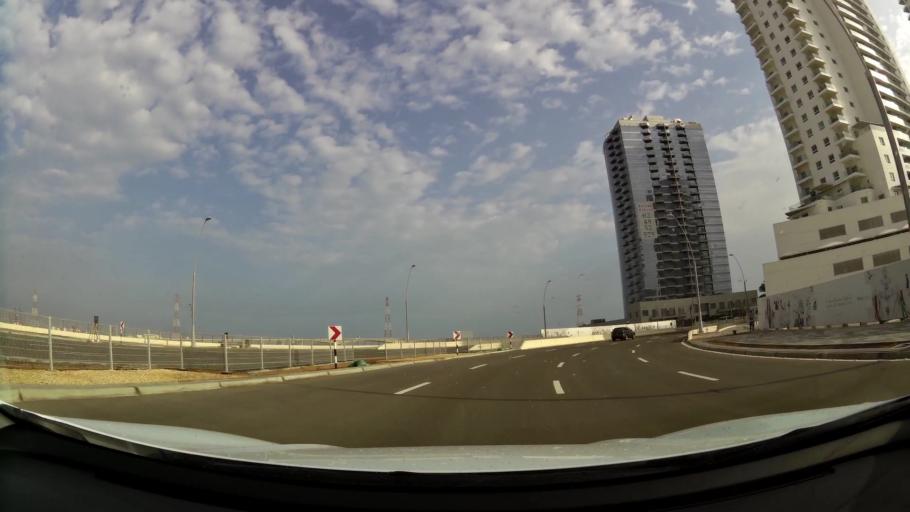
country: AE
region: Abu Dhabi
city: Abu Dhabi
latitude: 24.5107
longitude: 54.4048
